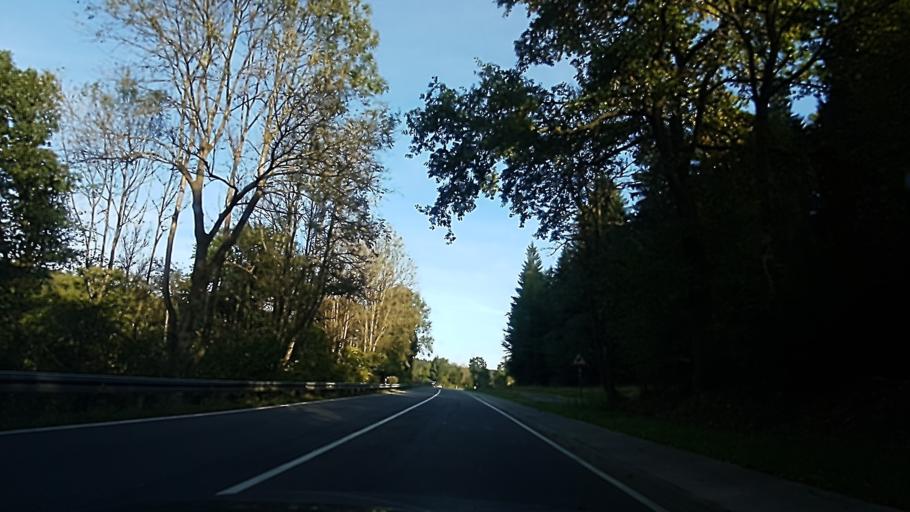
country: DE
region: North Rhine-Westphalia
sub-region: Regierungsbezirk Koln
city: Marienheide
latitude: 51.0998
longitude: 7.5072
